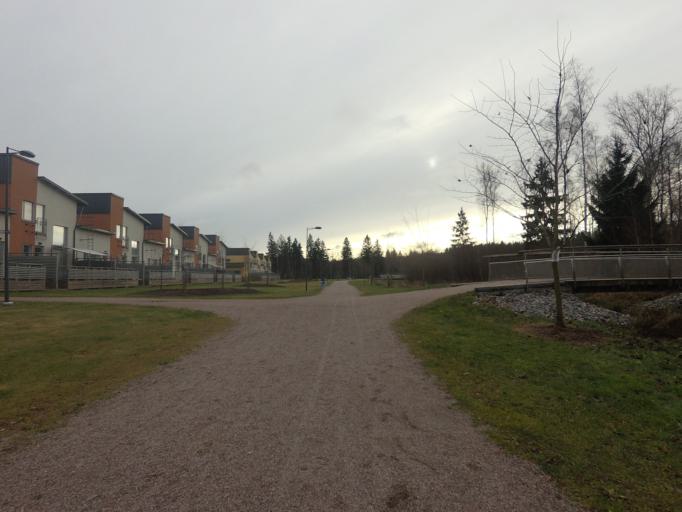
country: FI
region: Uusimaa
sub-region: Helsinki
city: Kauniainen
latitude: 60.1882
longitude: 24.7371
